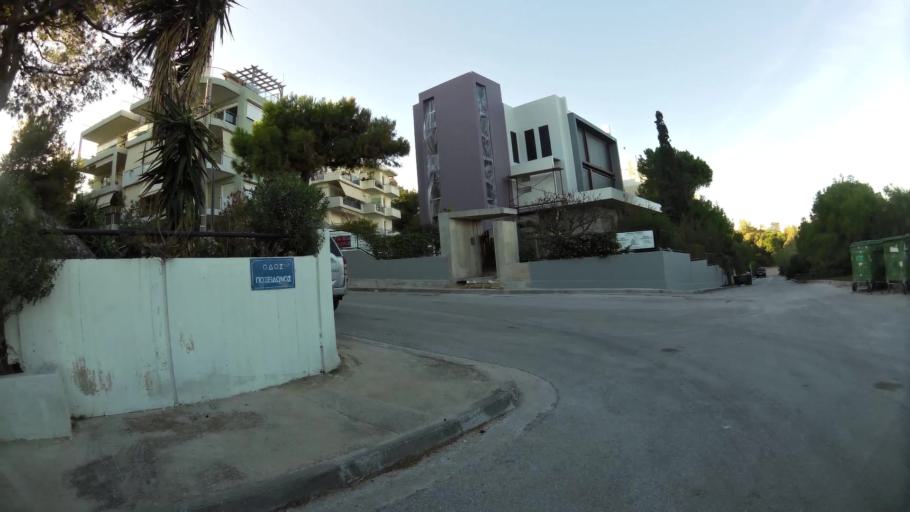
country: GR
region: Attica
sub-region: Nomarchia Anatolikis Attikis
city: Rafina
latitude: 38.0105
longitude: 24.0179
